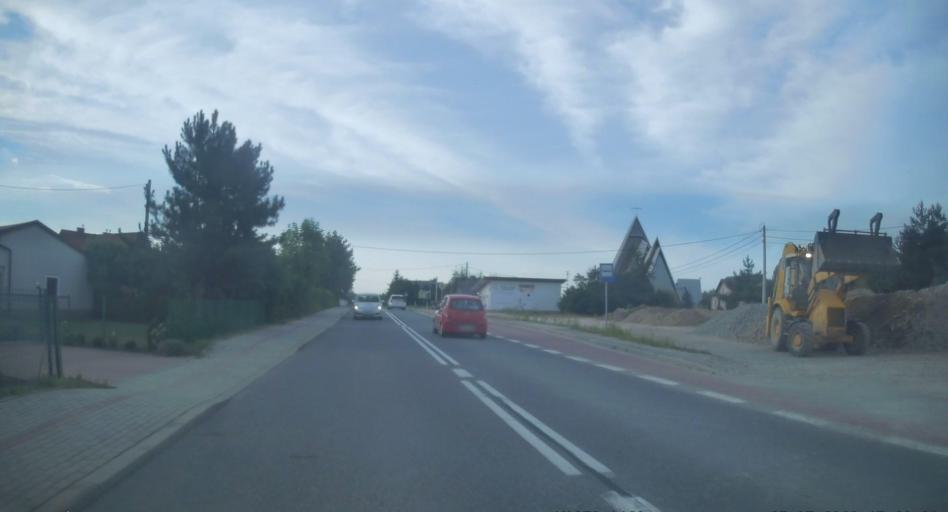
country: PL
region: Lesser Poland Voivodeship
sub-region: Powiat brzeski
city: Przyborow
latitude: 50.0620
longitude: 20.6381
